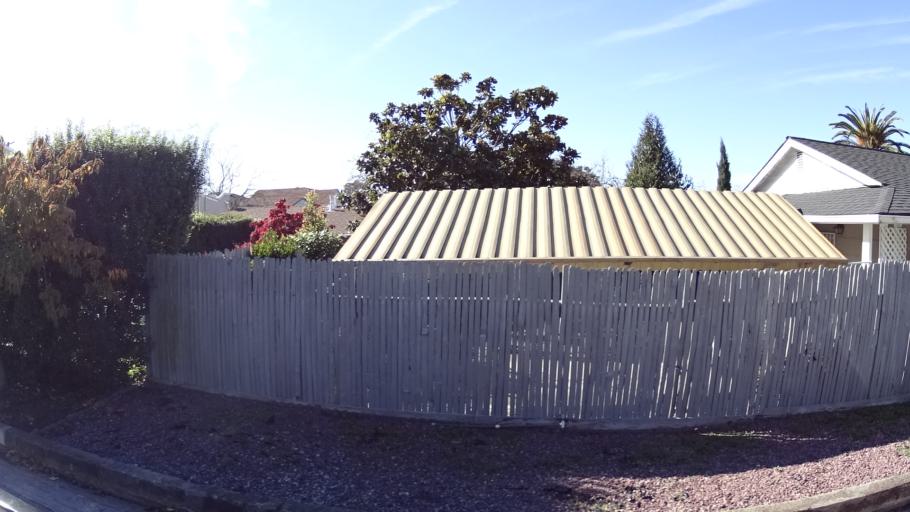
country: US
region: California
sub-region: Alameda County
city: Piedmont
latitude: 37.8244
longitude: -122.2399
